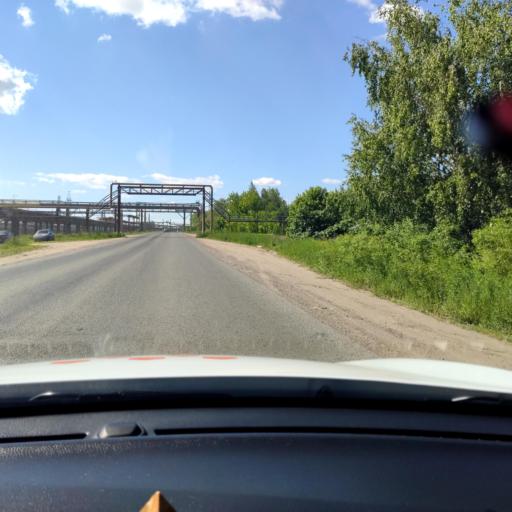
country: RU
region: Tatarstan
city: Staroye Arakchino
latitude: 55.8810
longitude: 48.9761
